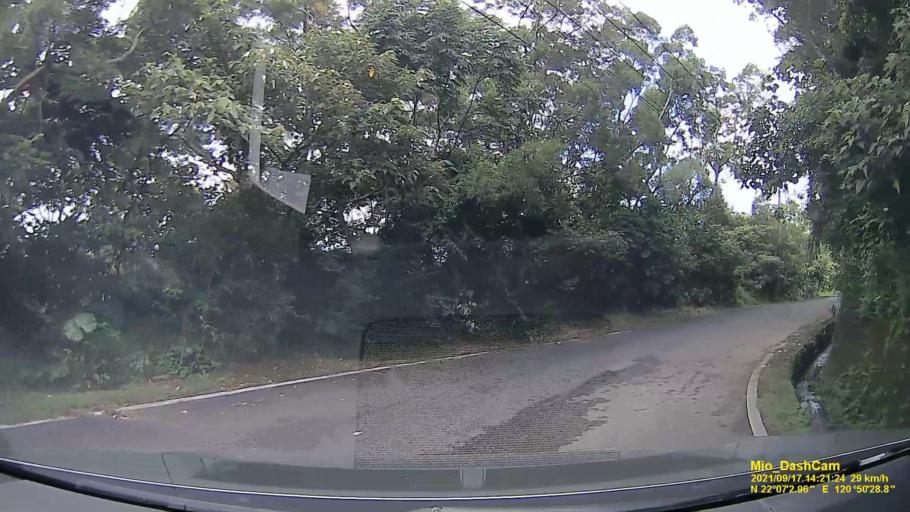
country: TW
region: Taiwan
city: Hengchun
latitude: 22.1175
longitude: 120.8414
